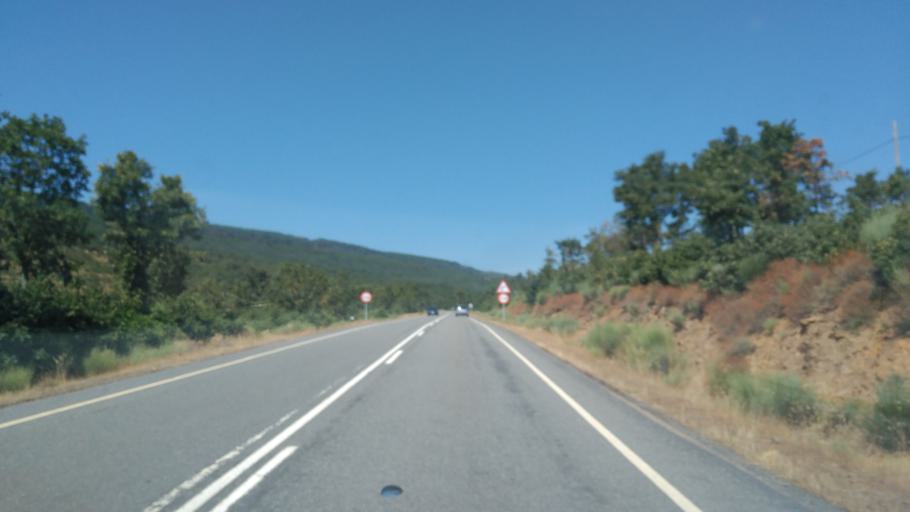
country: ES
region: Castille and Leon
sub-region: Provincia de Salamanca
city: Cereceda de la Sierra
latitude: 40.5809
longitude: -6.0799
